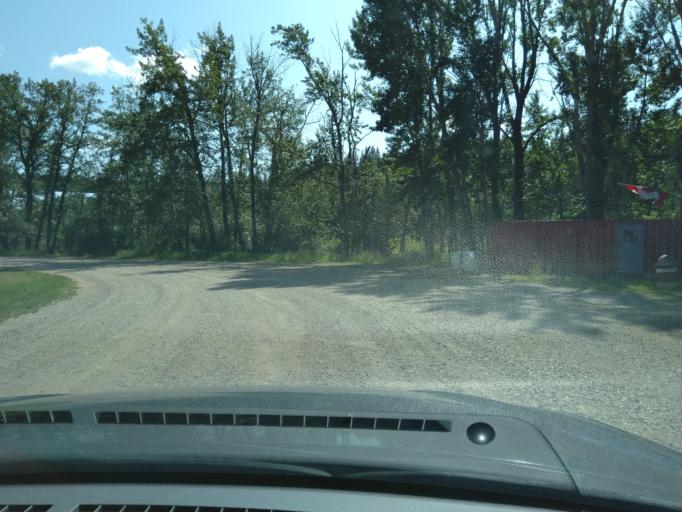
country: CA
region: Alberta
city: Calgary
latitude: 51.0983
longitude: -114.2367
